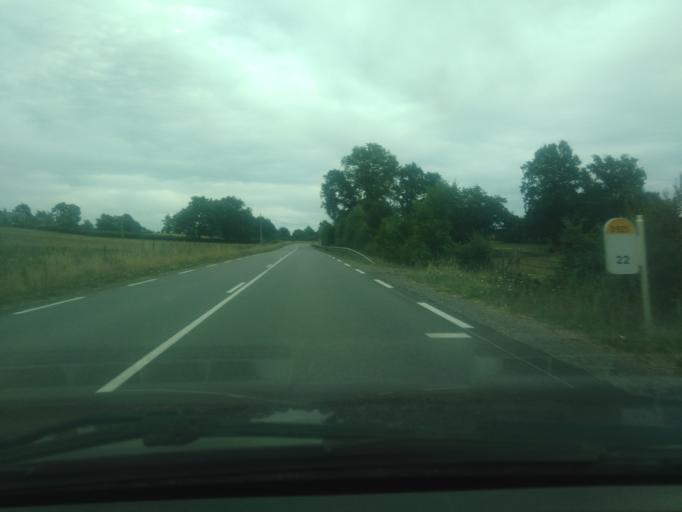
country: FR
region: Centre
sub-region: Departement du Cher
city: Lignieres
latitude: 46.7524
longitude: 2.2053
